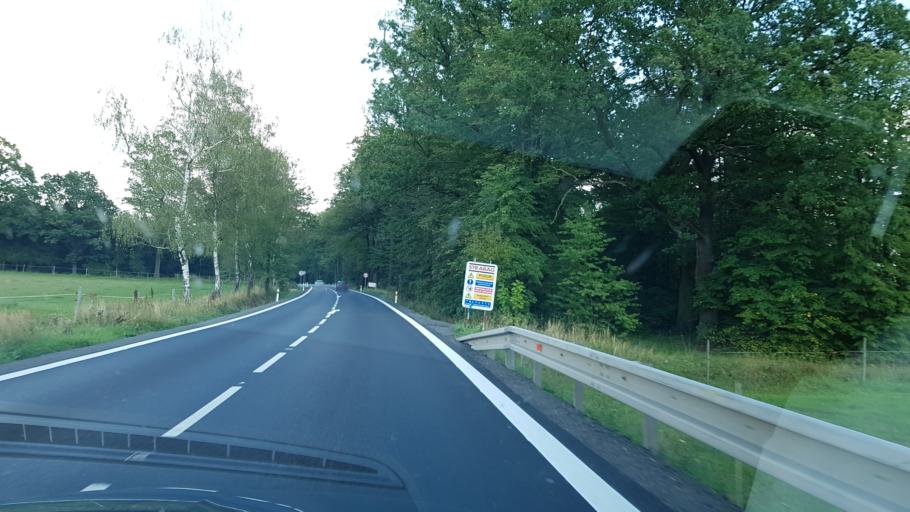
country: CZ
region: Pardubicky
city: Zamberk
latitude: 50.0973
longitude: 16.4098
